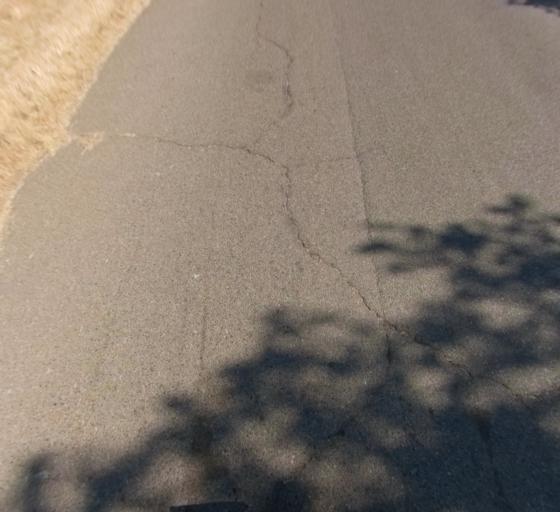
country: US
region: California
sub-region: Madera County
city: Parkwood
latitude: 36.9350
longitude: -120.0558
